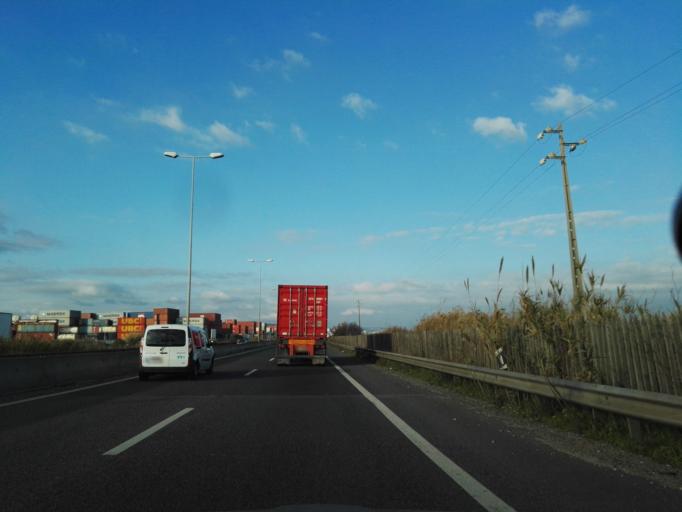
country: PT
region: Lisbon
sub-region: Loures
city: Bobadela
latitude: 38.8036
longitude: -9.0916
